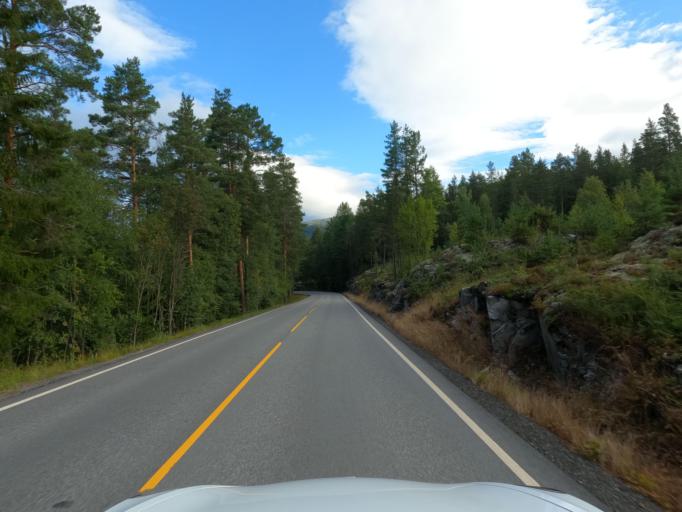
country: NO
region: Telemark
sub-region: Notodden
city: Notodden
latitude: 59.7339
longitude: 9.1584
